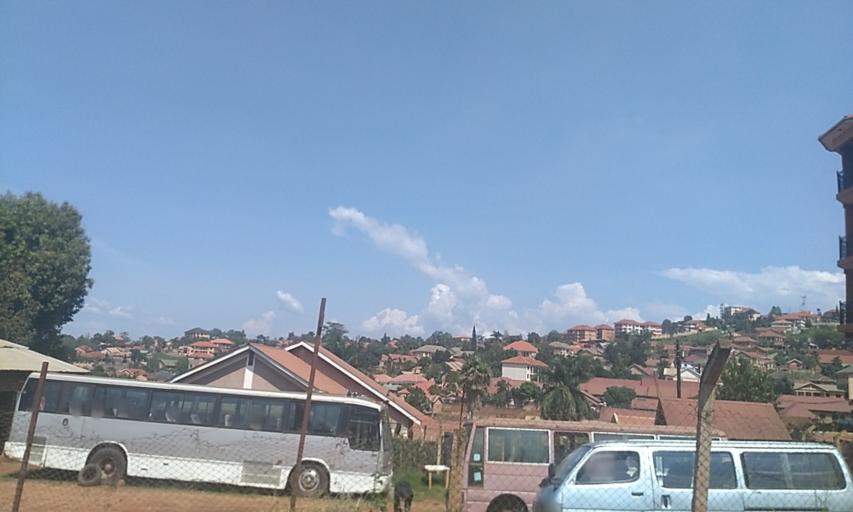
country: UG
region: Central Region
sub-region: Wakiso District
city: Kireka
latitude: 0.3726
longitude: 32.6016
